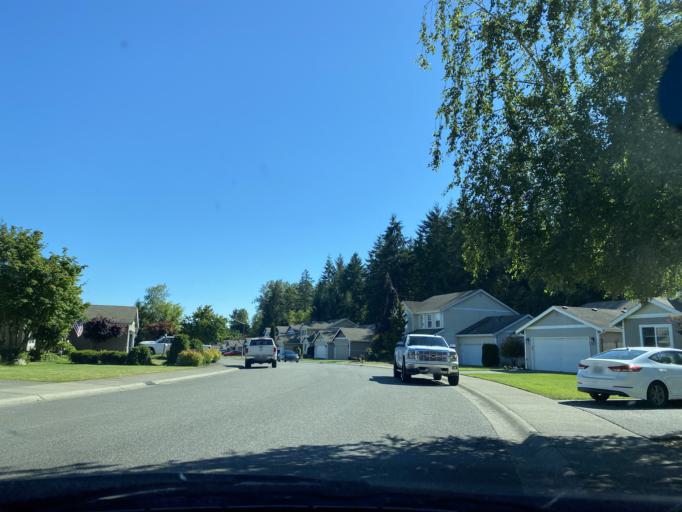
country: US
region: Washington
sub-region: Pierce County
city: South Hill
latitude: 47.1029
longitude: -122.2580
